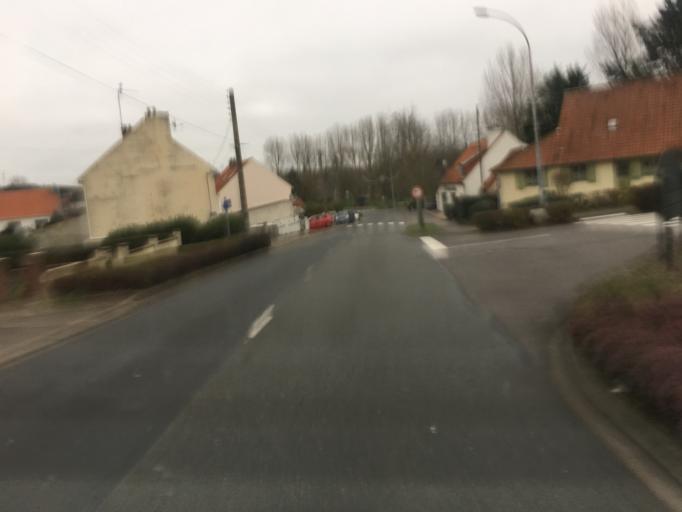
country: FR
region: Nord-Pas-de-Calais
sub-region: Departement du Pas-de-Calais
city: Wimille
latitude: 50.7645
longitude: 1.6262
